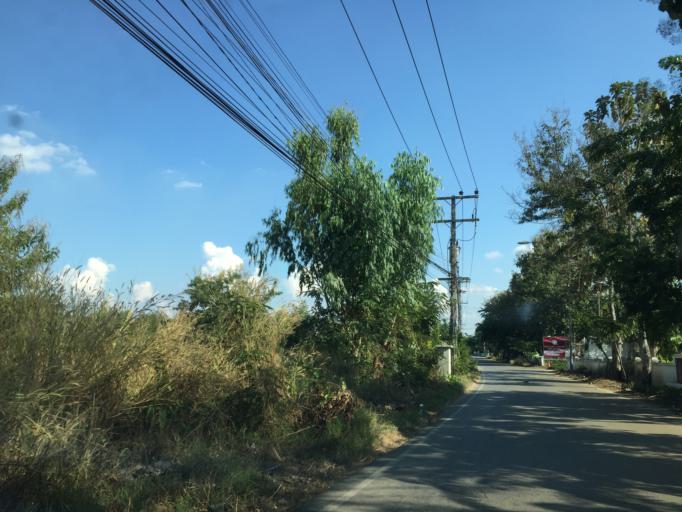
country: TH
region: Lamphun
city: Lamphun
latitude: 18.5714
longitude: 99.0391
